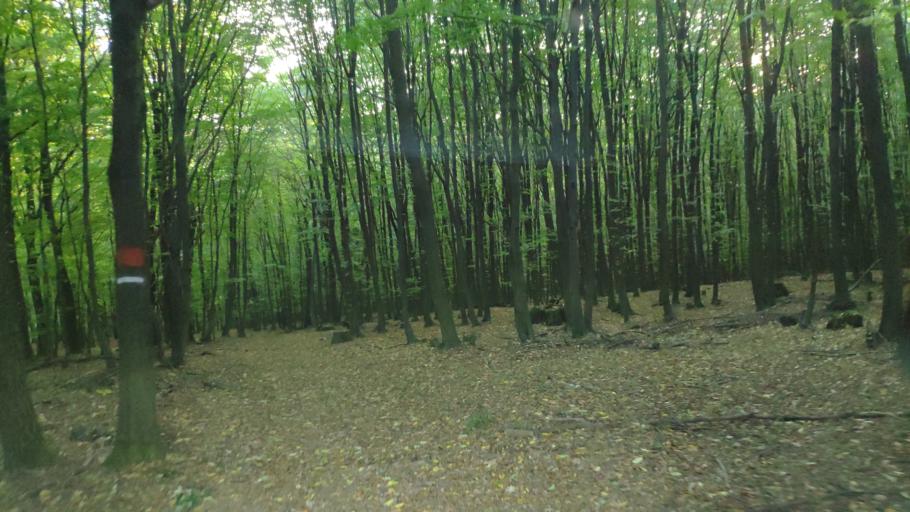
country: SK
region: Kosicky
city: Kosice
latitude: 48.7062
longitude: 21.1954
